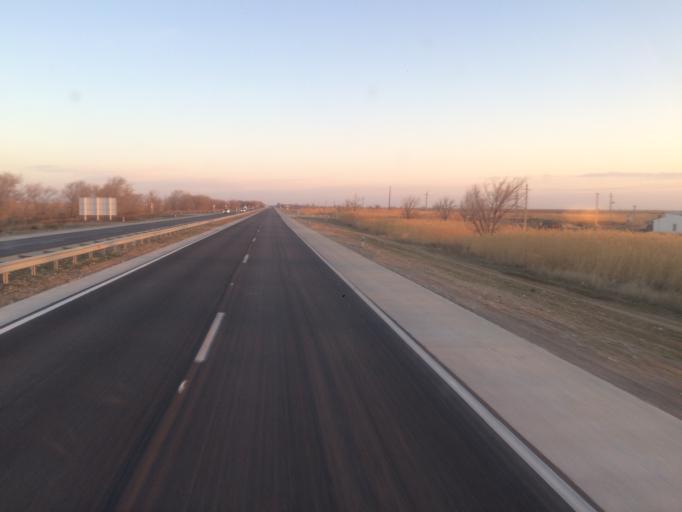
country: KZ
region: Ongtustik Qazaqstan
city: Bayaldyr
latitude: 43.0956
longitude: 68.6340
